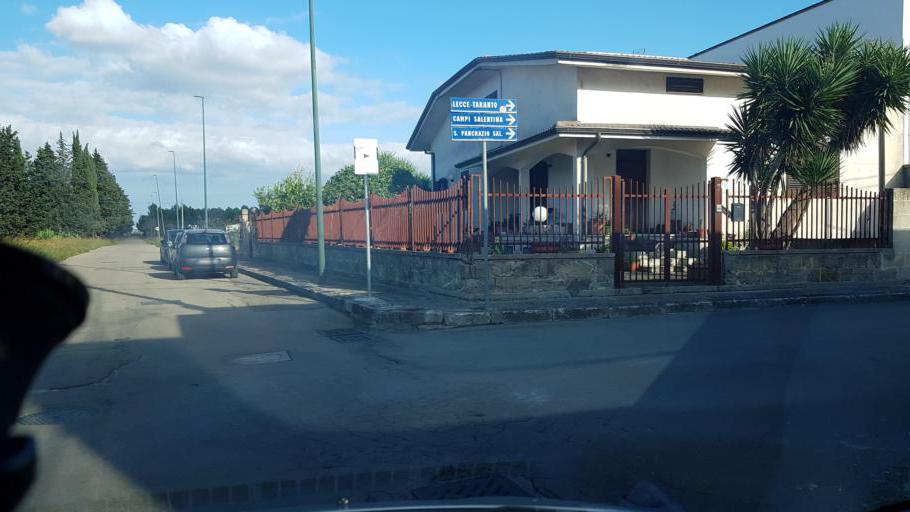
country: IT
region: Apulia
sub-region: Provincia di Lecce
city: Guagnano
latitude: 40.4024
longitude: 17.9549
